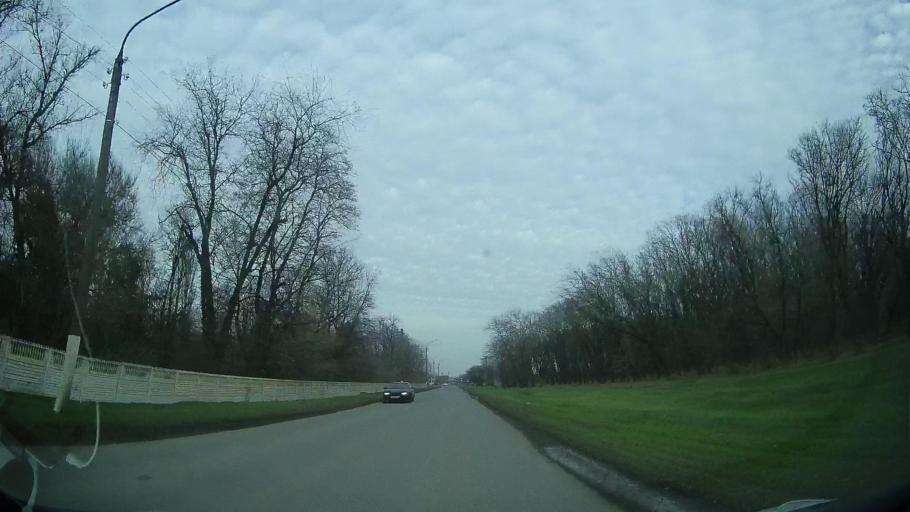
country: RU
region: Rostov
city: Zernograd
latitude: 46.8560
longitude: 40.3172
